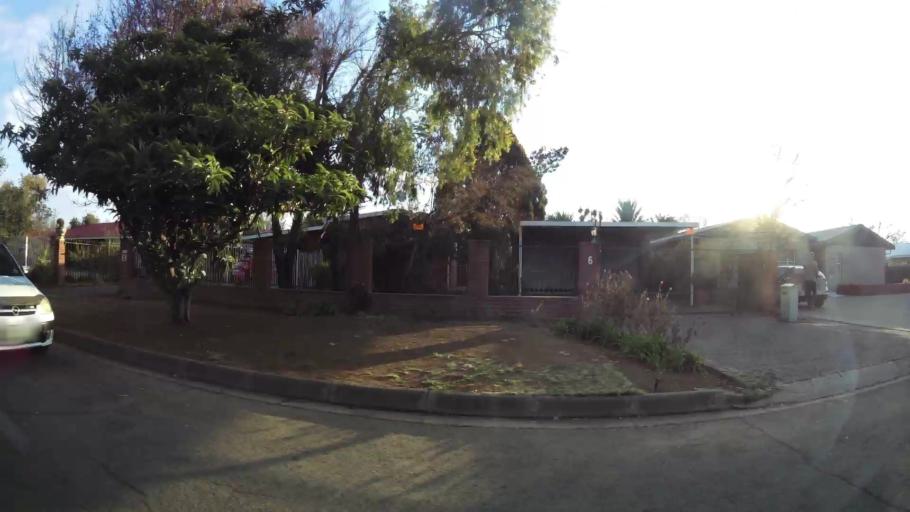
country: ZA
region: Orange Free State
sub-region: Mangaung Metropolitan Municipality
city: Bloemfontein
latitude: -29.1343
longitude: 26.1925
